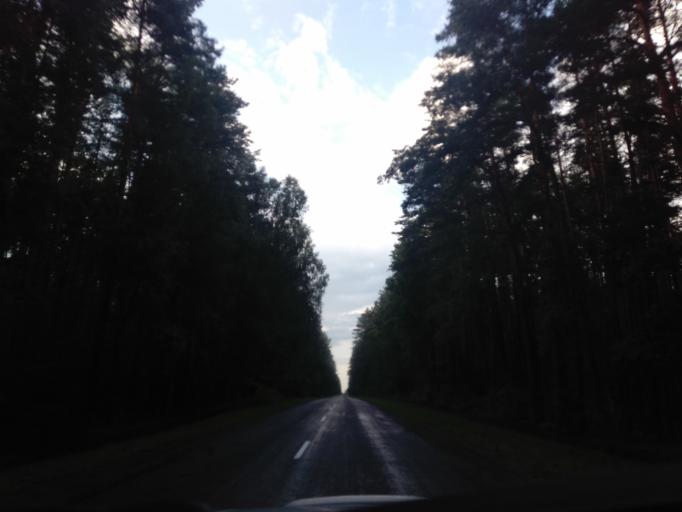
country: BY
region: Minsk
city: Uzda
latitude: 53.3644
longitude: 27.1017
